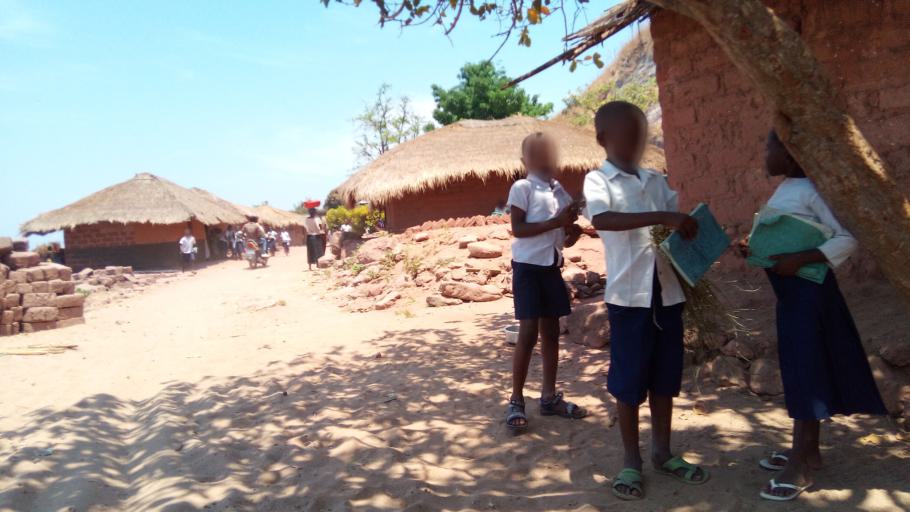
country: CD
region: Katanga
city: Kalemie
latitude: -5.9898
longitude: 29.1937
